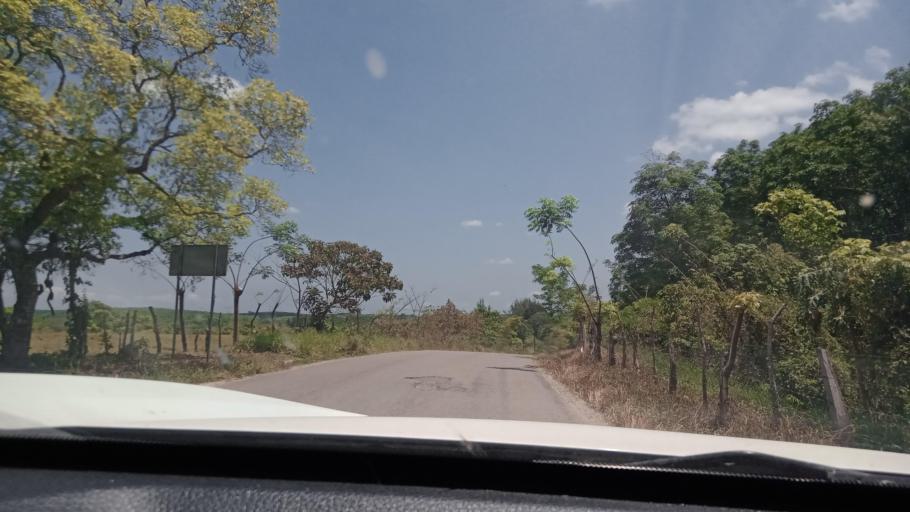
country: MX
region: Veracruz
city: Las Choapas
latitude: 17.7566
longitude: -94.1115
